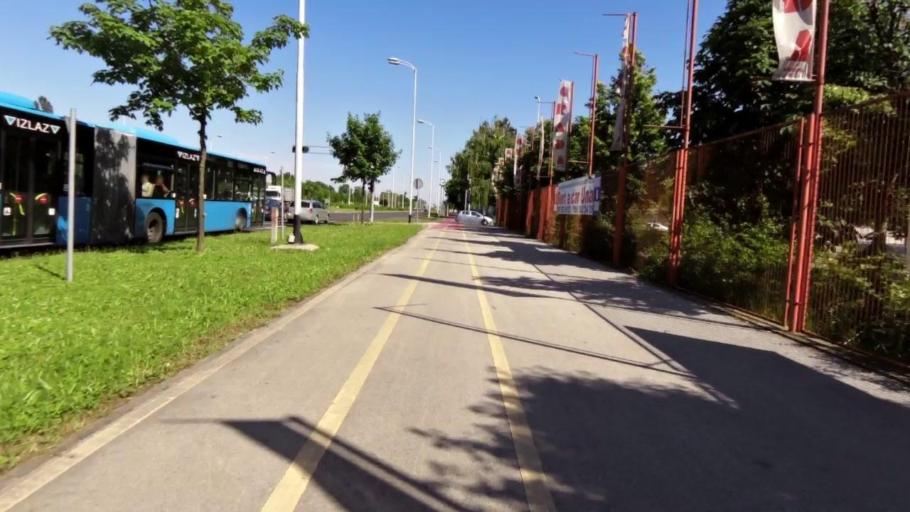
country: HR
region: Grad Zagreb
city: Novi Zagreb
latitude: 45.7926
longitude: 16.0260
